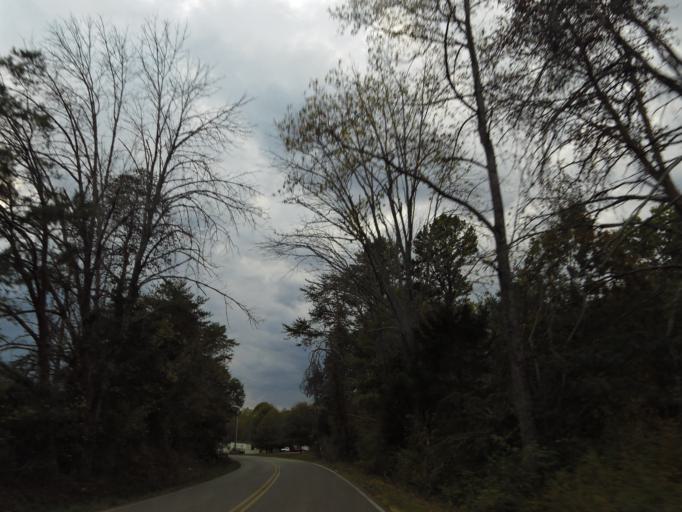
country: US
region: Tennessee
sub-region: Blount County
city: Louisville
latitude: 35.7797
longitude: -84.0843
